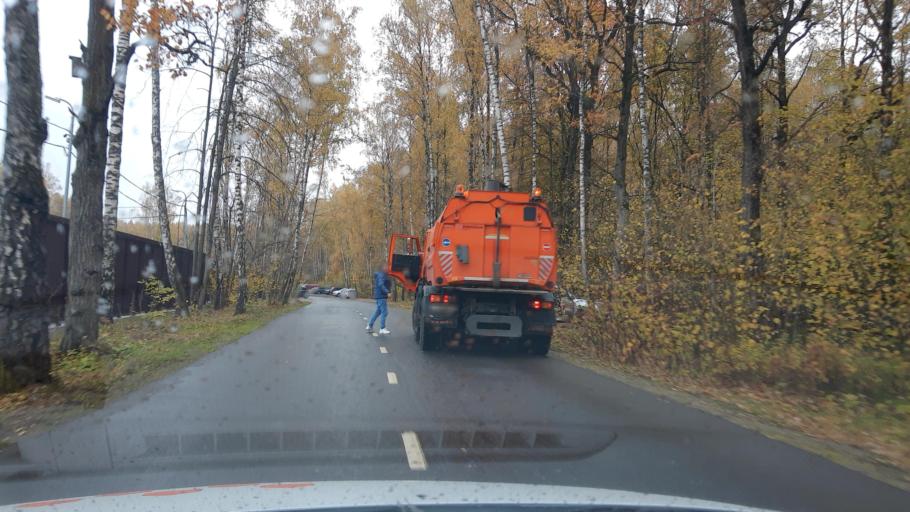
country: RU
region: Moskovskaya
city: Shcherbinka
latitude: 55.5304
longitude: 37.5638
